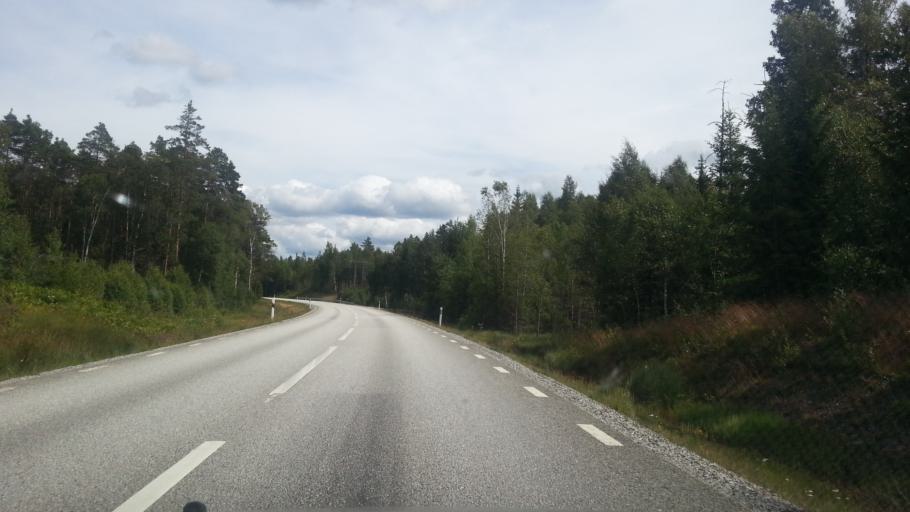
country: SE
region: Vaestmanland
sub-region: Skinnskattebergs Kommun
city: Skinnskatteberg
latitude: 59.7676
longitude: 15.5107
